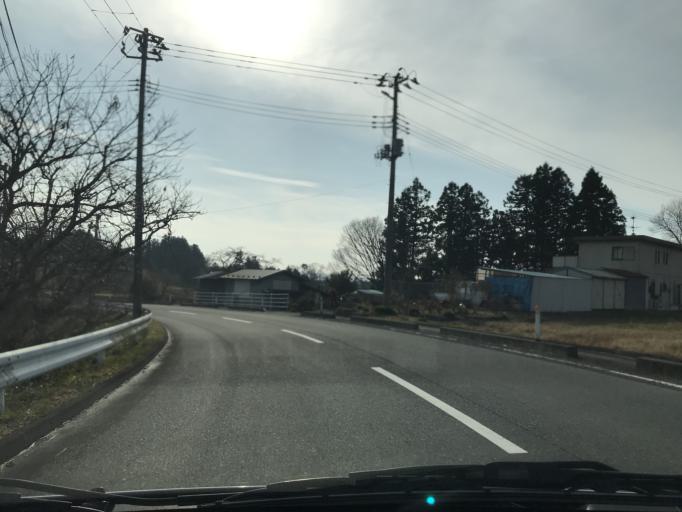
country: JP
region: Miyagi
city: Wakuya
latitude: 38.6980
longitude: 141.1537
